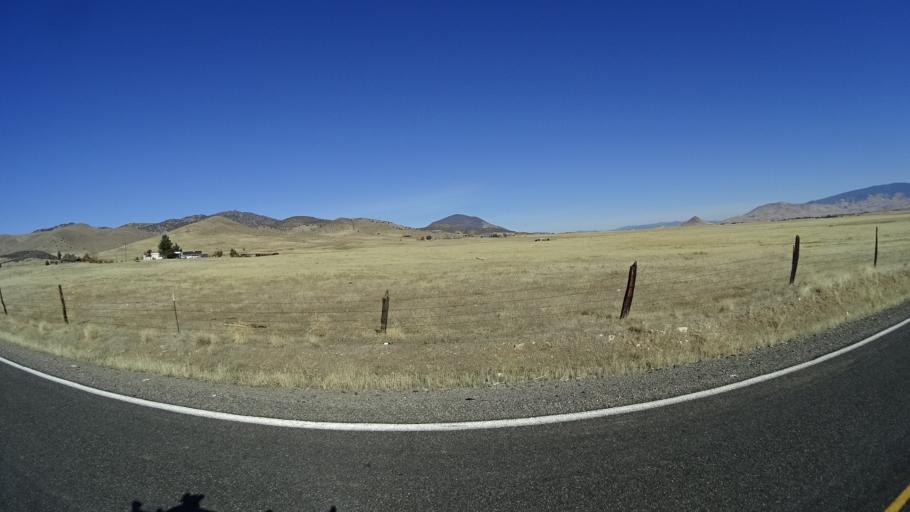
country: US
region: California
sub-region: Siskiyou County
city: Montague
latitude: 41.7708
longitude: -122.5192
